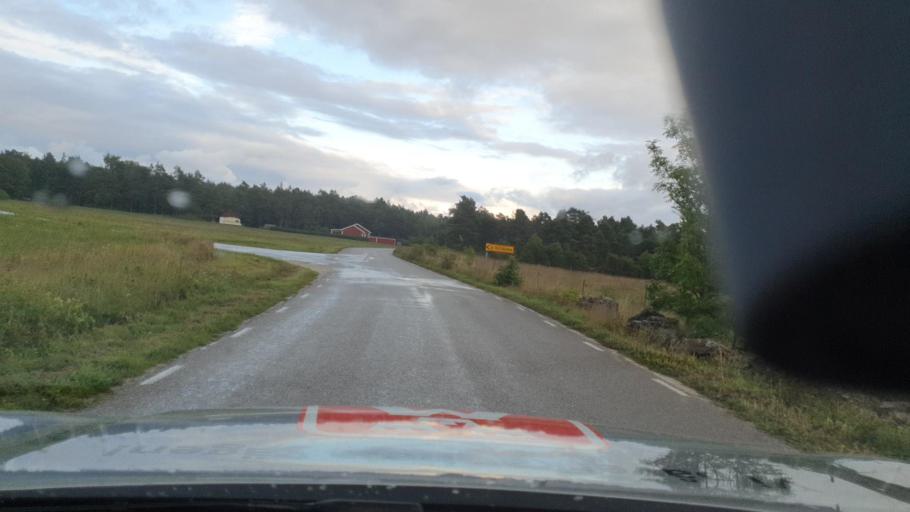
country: SE
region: Gotland
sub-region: Gotland
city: Vibble
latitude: 57.5313
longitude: 18.2372
